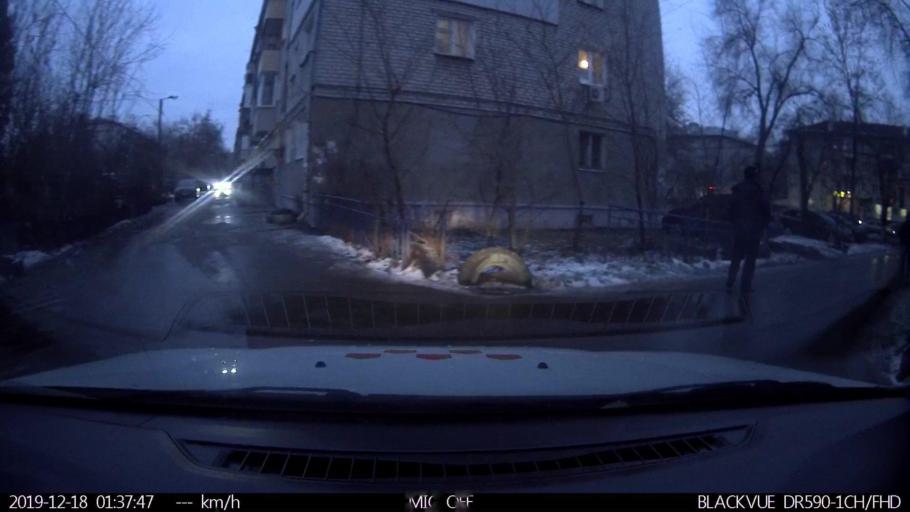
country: RU
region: Nizjnij Novgorod
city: Nizhniy Novgorod
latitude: 56.3208
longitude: 43.8885
